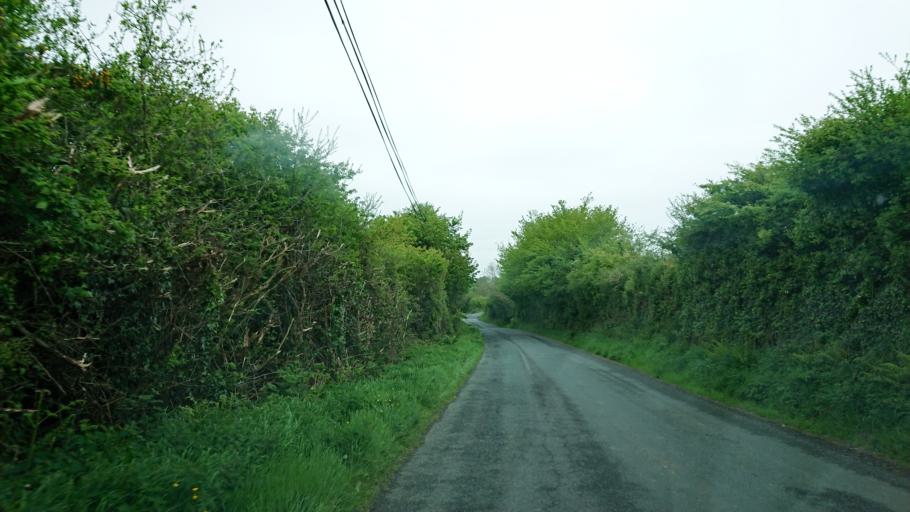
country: IE
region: Munster
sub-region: Waterford
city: Waterford
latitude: 52.2246
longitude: -7.0355
